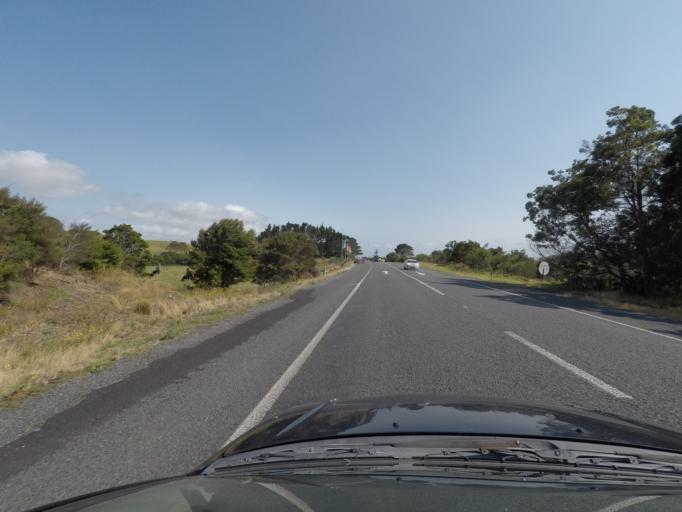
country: NZ
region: Northland
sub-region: Whangarei
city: Ruakaka
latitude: -35.9376
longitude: 174.4559
